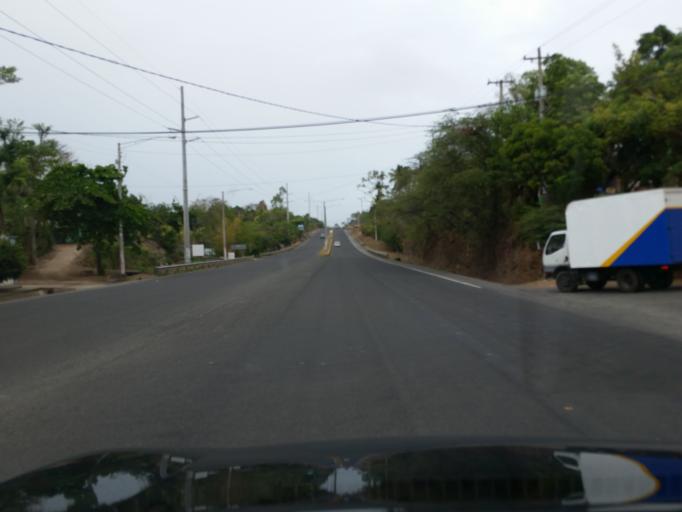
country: NI
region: Masaya
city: Masaya
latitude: 11.9729
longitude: -86.0263
